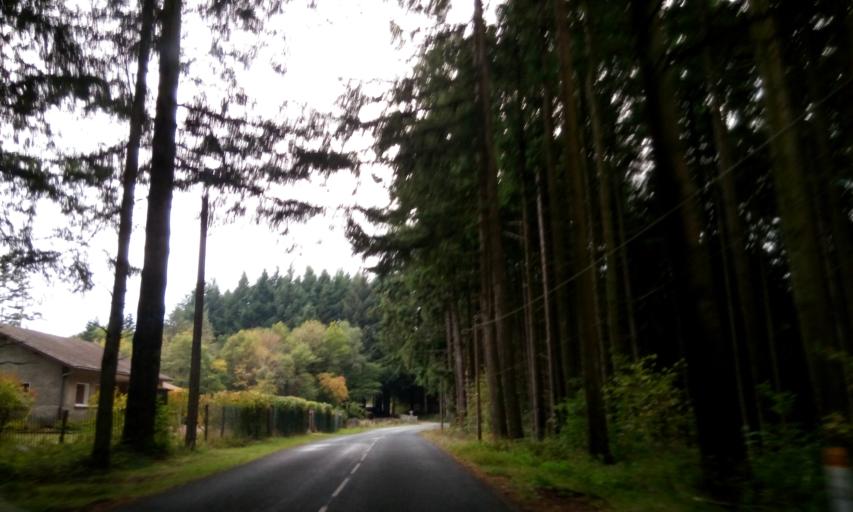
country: FR
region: Rhone-Alpes
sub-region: Departement du Rhone
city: Grandris
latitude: 46.0340
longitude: 4.4315
